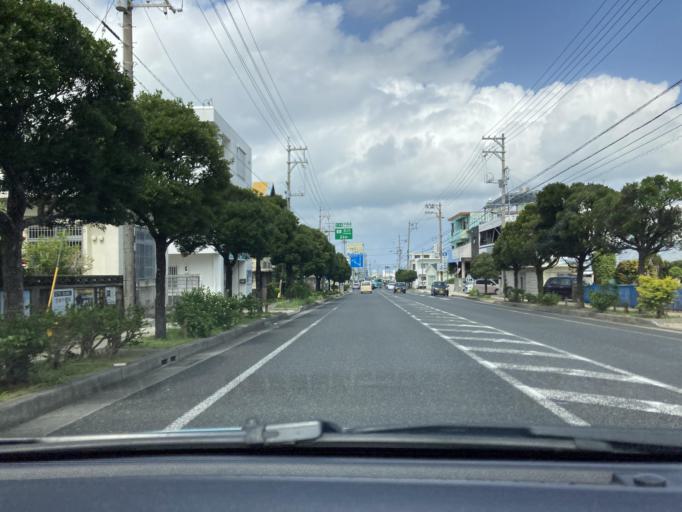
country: JP
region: Okinawa
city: Ishikawa
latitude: 26.4097
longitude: 127.8281
